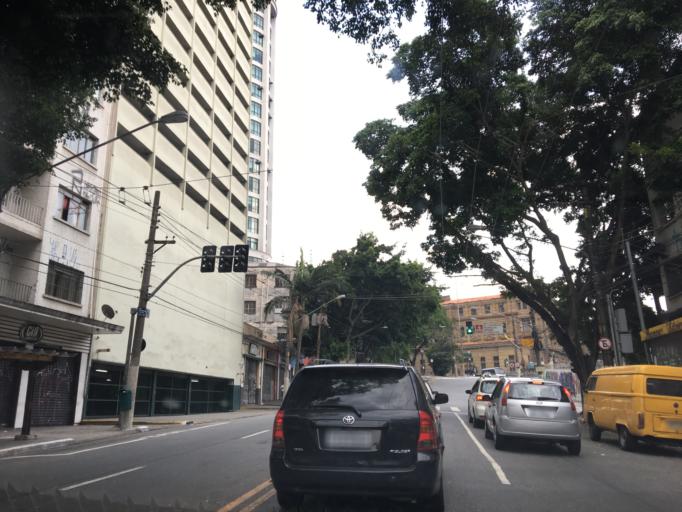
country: BR
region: Sao Paulo
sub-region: Sao Paulo
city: Sao Paulo
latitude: -23.5539
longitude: -46.6332
